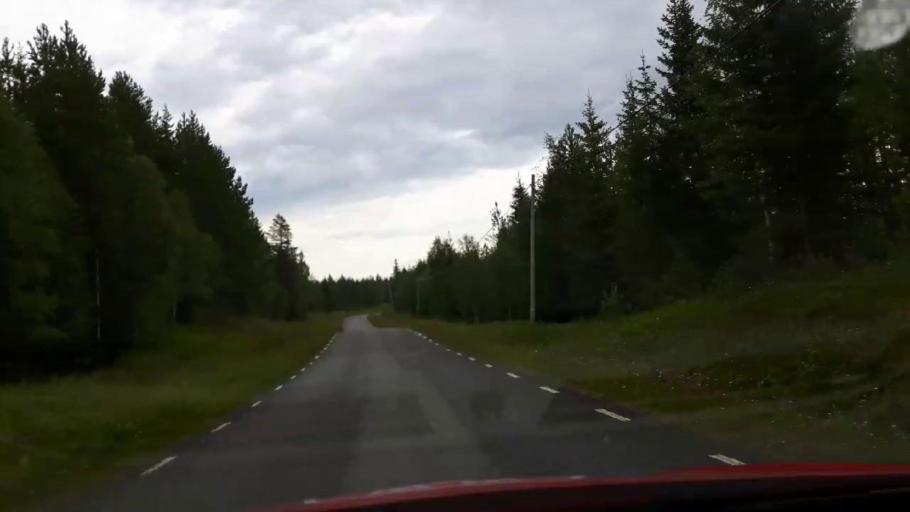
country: SE
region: Jaemtland
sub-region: OEstersunds Kommun
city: Lit
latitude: 63.3788
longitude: 15.0708
